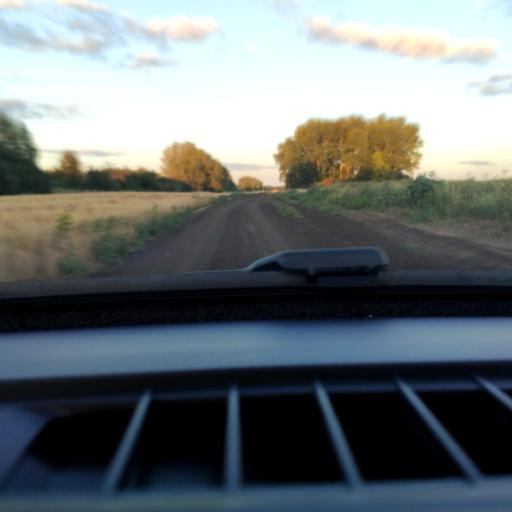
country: RU
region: Voronezj
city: Verkhnyaya Khava
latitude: 51.5913
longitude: 39.8555
